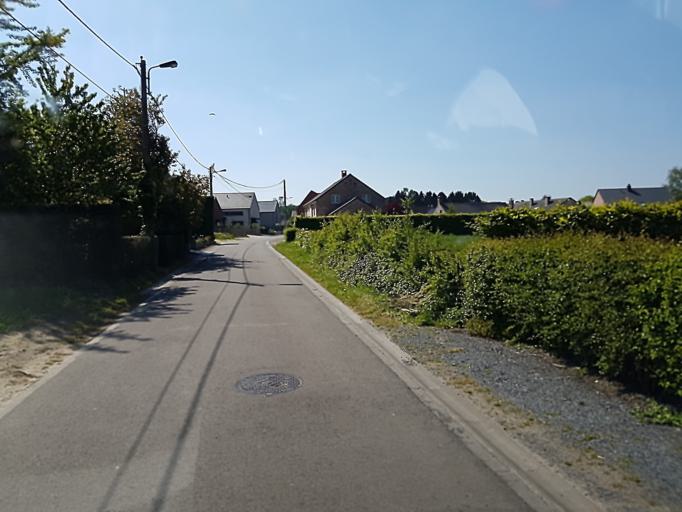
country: BE
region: Wallonia
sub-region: Province du Hainaut
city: Jurbise
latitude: 50.5108
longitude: 3.9057
